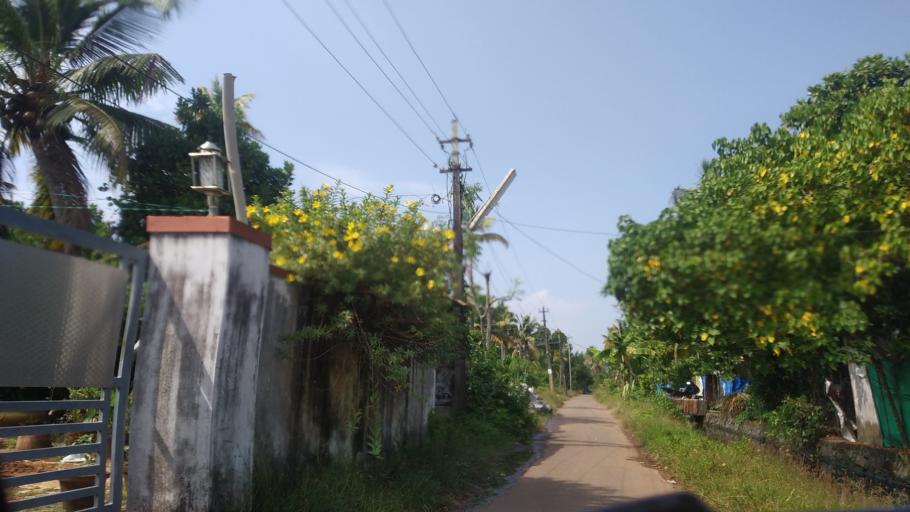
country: IN
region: Kerala
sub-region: Ernakulam
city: Elur
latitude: 10.0808
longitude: 76.2036
